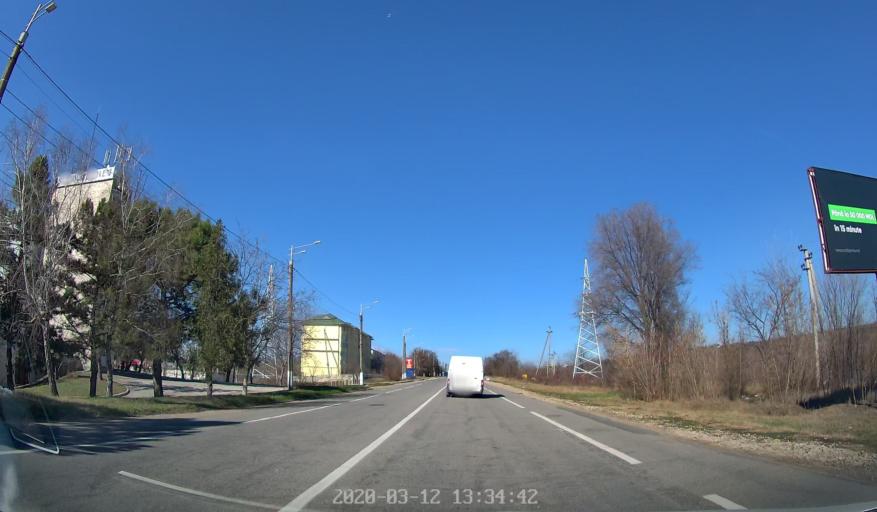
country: MD
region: Laloveni
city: Ialoveni
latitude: 46.9656
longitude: 28.7669
